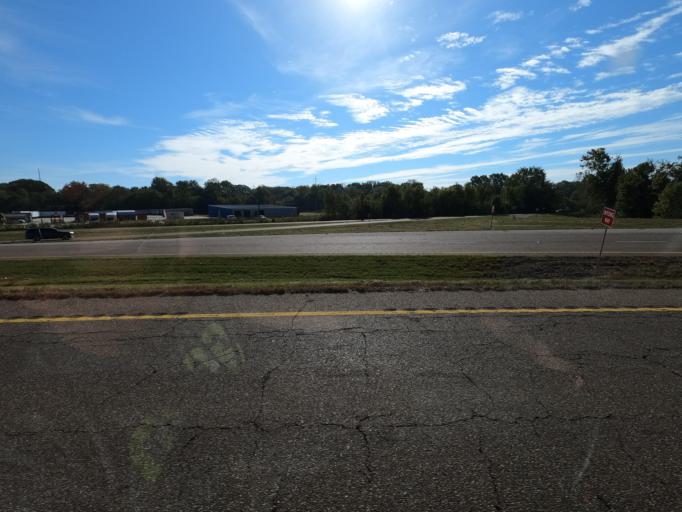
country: US
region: Tennessee
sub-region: Tipton County
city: Brighton
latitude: 35.4927
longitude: -89.7253
